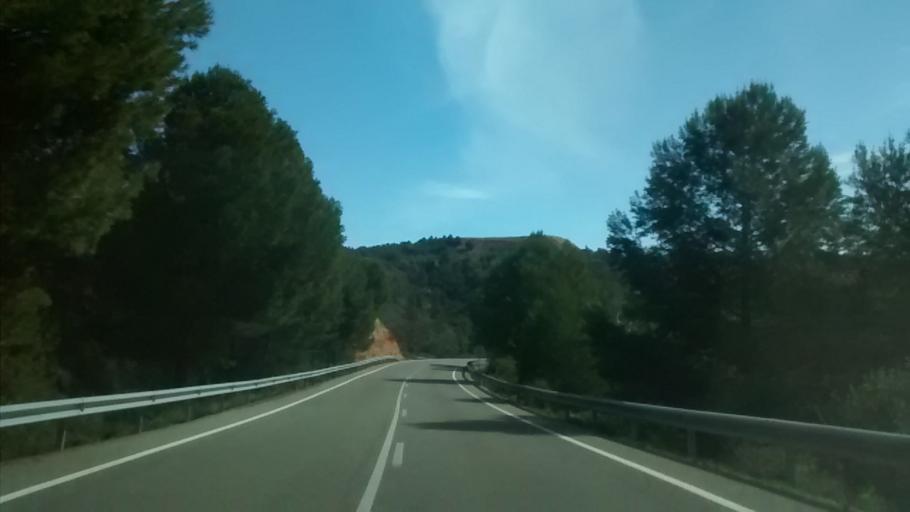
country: ES
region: Catalonia
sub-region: Provincia de Lleida
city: Maials
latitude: 41.3191
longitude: 0.5188
